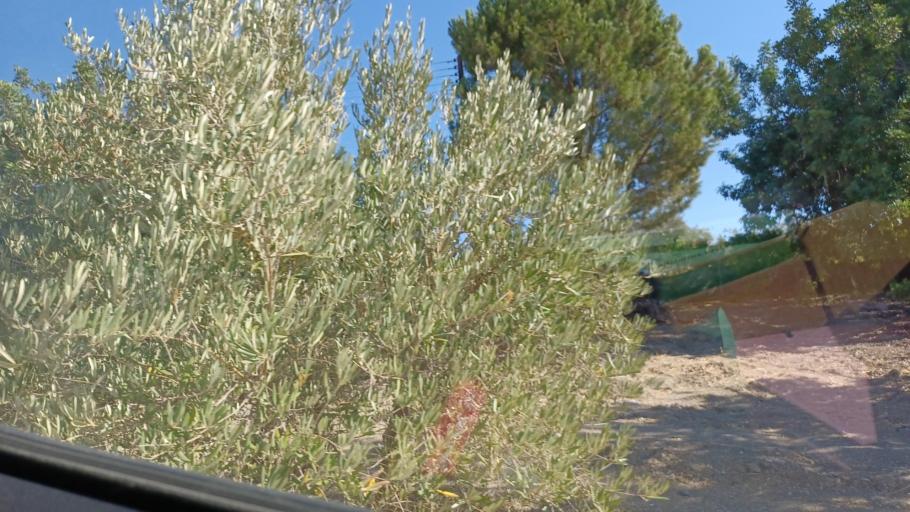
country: CY
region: Pafos
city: Polis
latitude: 34.9848
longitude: 32.4746
